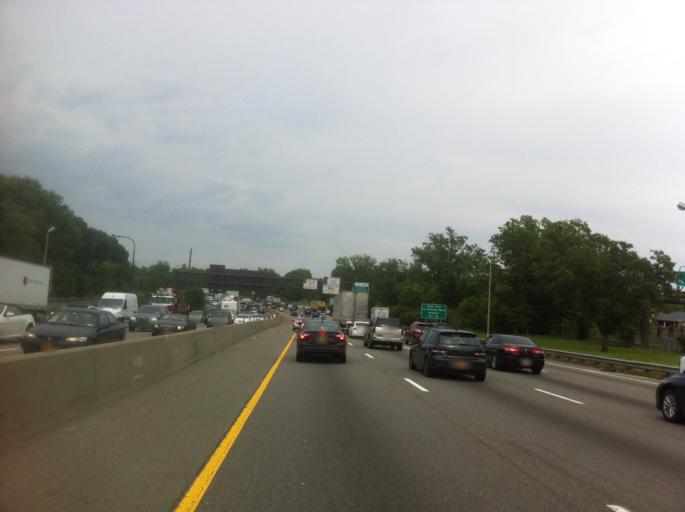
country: US
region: New York
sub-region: Nassau County
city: Lake Success
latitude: 40.7643
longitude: -73.7236
